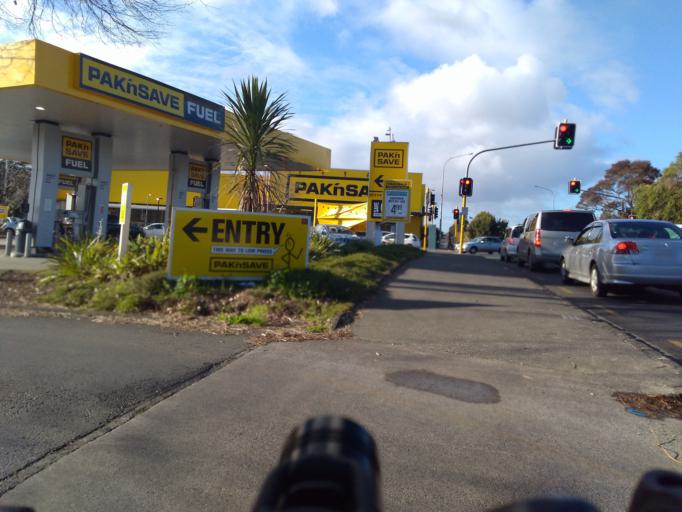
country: NZ
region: Auckland
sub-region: Auckland
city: Rosebank
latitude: -36.8938
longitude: 174.7055
